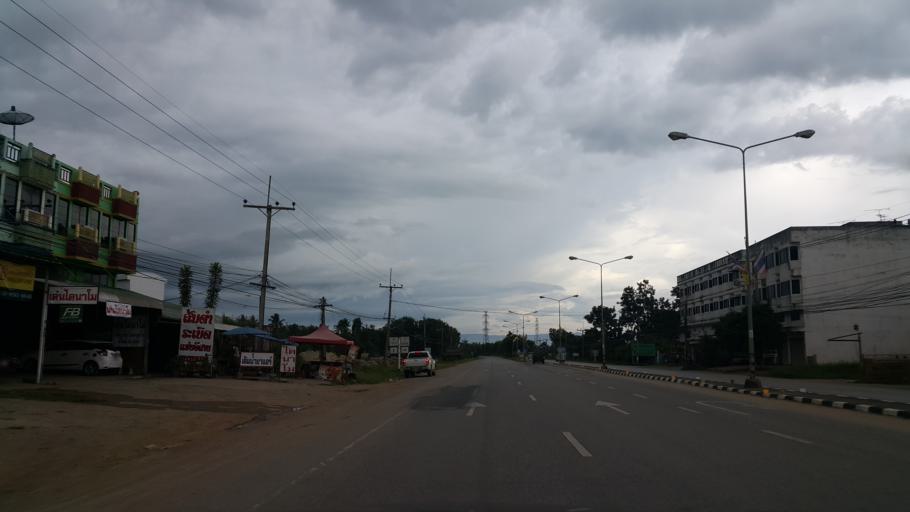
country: TH
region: Phayao
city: Phayao
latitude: 19.1432
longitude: 99.9224
